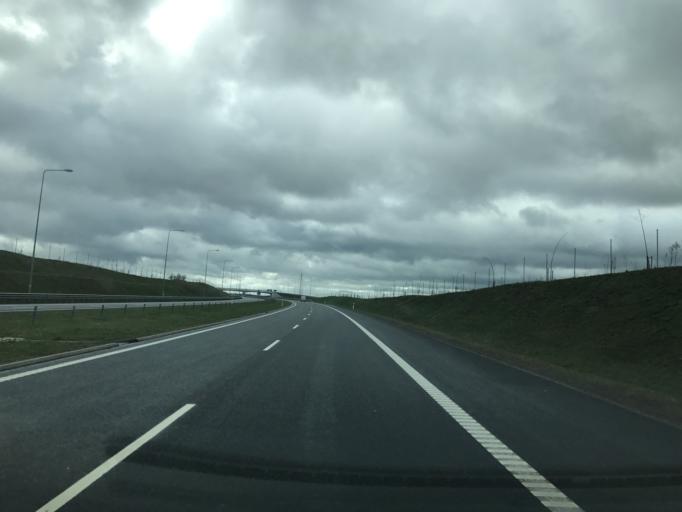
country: PL
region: Warmian-Masurian Voivodeship
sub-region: Powiat olsztynski
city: Olsztynek
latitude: 53.5954
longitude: 20.2636
